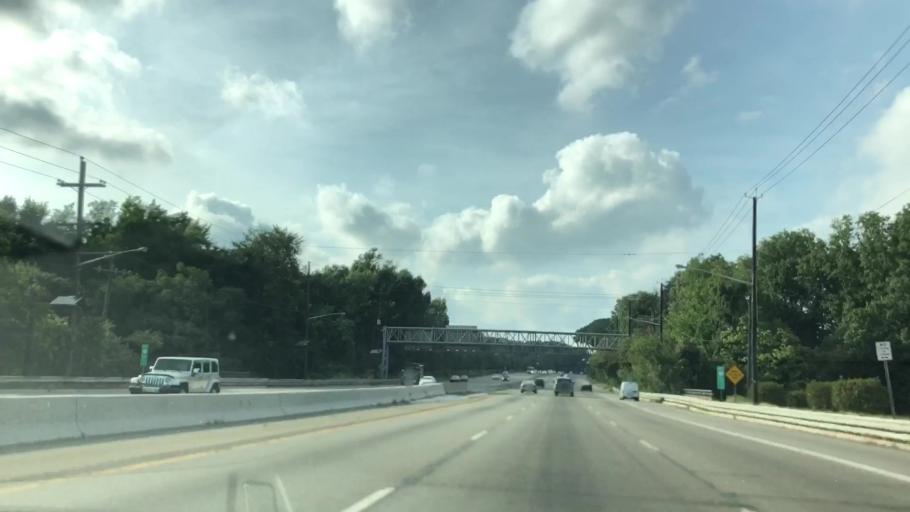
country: US
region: New Jersey
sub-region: Essex County
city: Nutley
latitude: 40.8402
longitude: -74.1604
